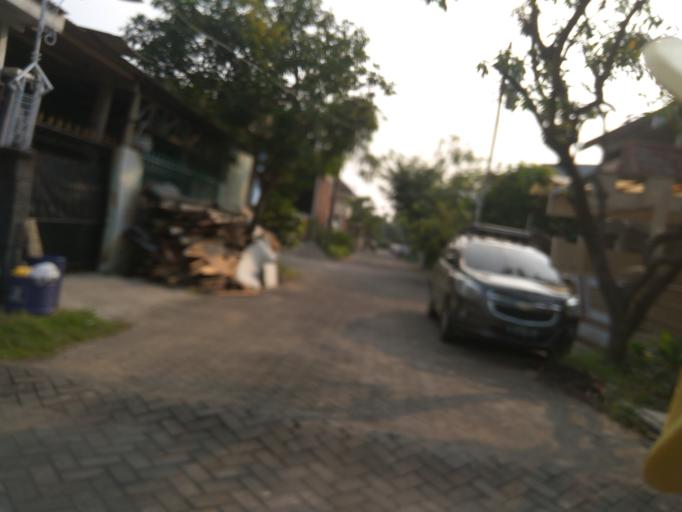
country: ID
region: Central Java
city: Semarang
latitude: -6.9697
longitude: 110.3985
